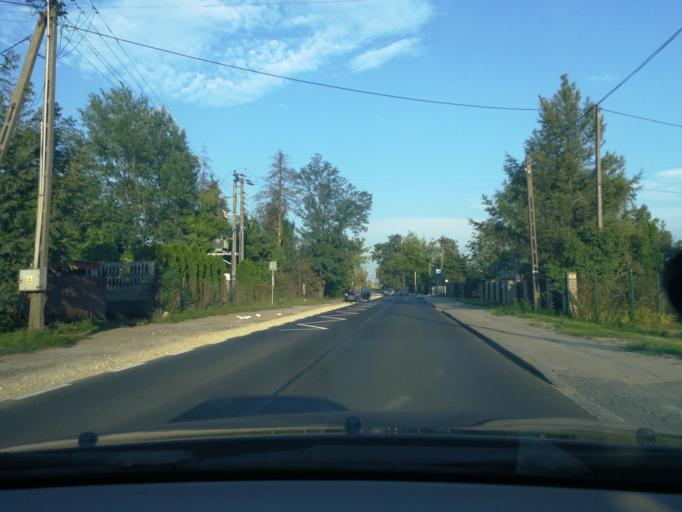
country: PL
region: Masovian Voivodeship
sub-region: Powiat warszawski zachodni
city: Ozarow Mazowiecki
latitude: 52.1866
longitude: 20.7665
